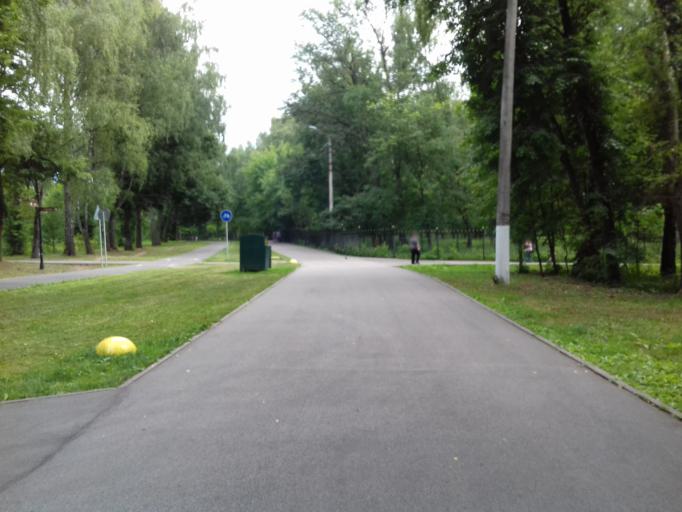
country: RU
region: Tula
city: Tula
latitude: 54.1791
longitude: 37.5830
